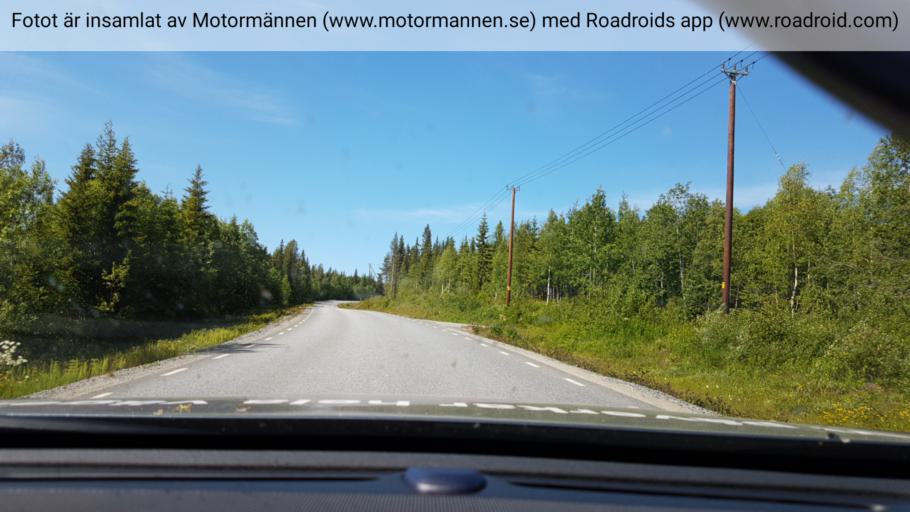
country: SE
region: Vaesterbotten
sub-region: Vilhelmina Kommun
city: Sjoberg
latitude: 64.7109
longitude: 15.4862
